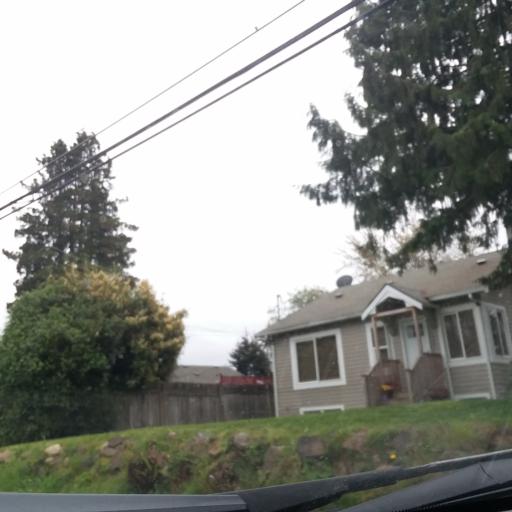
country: US
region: Washington
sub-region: King County
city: Boulevard Park
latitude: 47.4994
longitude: -122.3171
